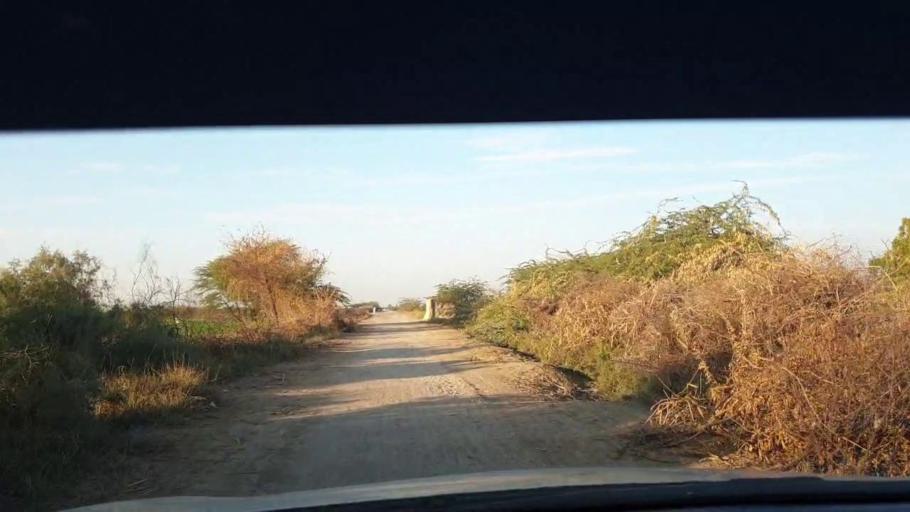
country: PK
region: Sindh
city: Berani
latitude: 25.8040
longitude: 68.8824
